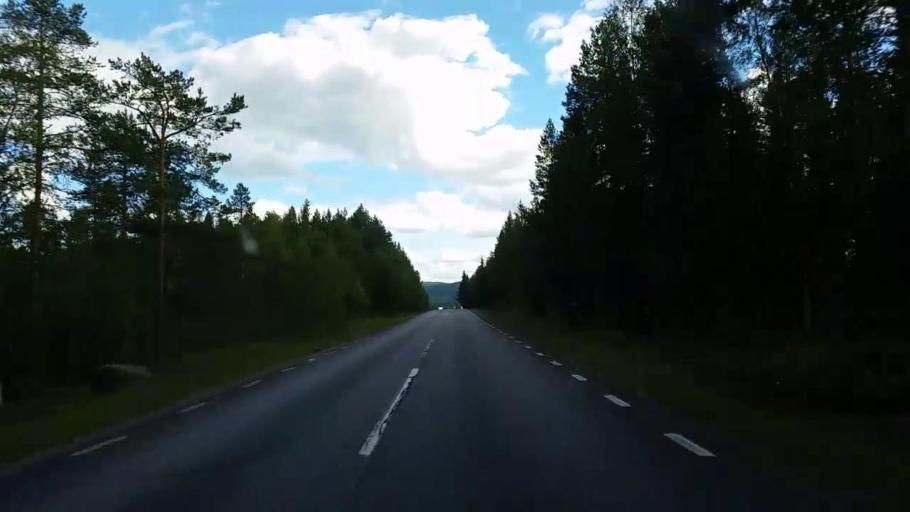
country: SE
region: Gaevleborg
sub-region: Ljusdals Kommun
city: Farila
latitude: 62.1420
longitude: 15.6873
